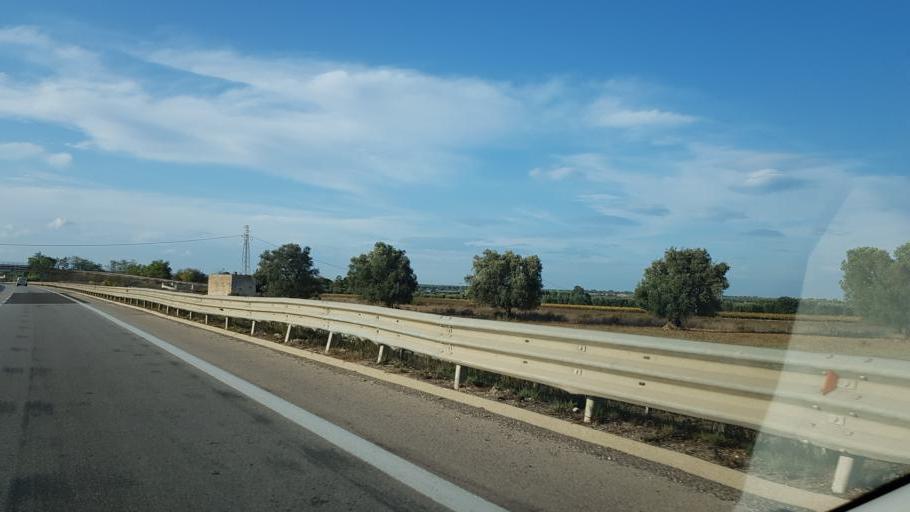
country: IT
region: Apulia
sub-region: Provincia di Brindisi
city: Francavilla Fontana
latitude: 40.5402
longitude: 17.6052
